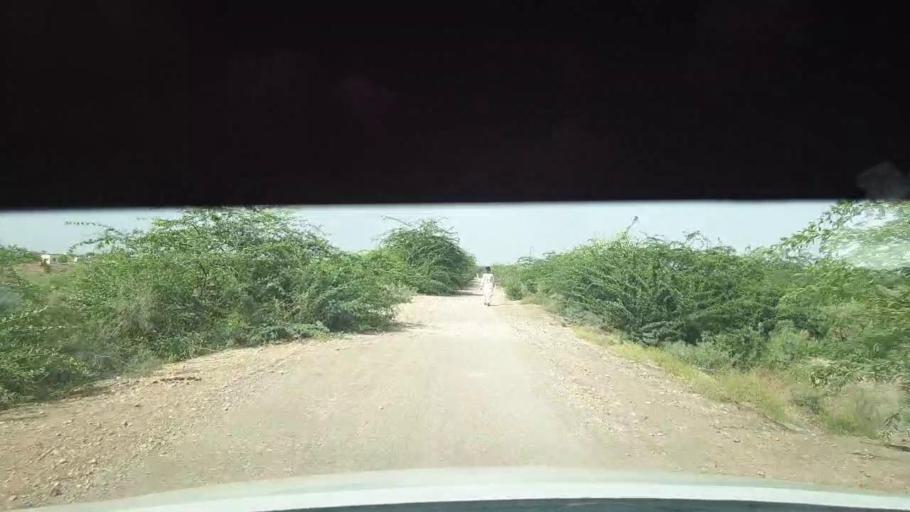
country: PK
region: Sindh
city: Kadhan
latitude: 24.5309
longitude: 69.0365
